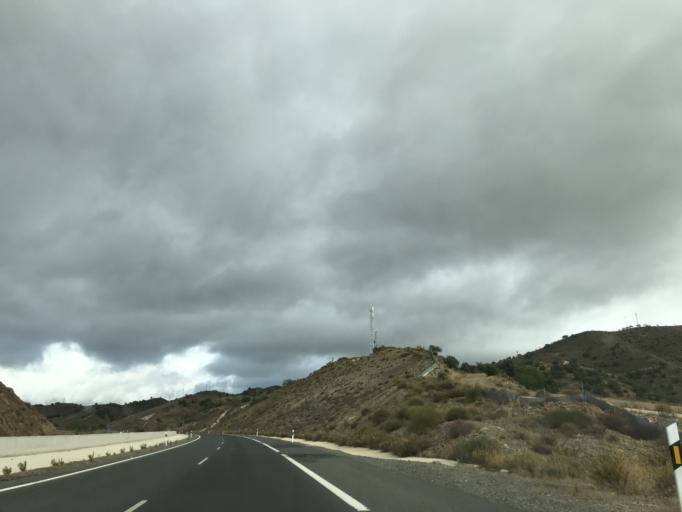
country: ES
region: Andalusia
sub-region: Provincia de Malaga
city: Almogia
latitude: 36.7897
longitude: -4.4691
